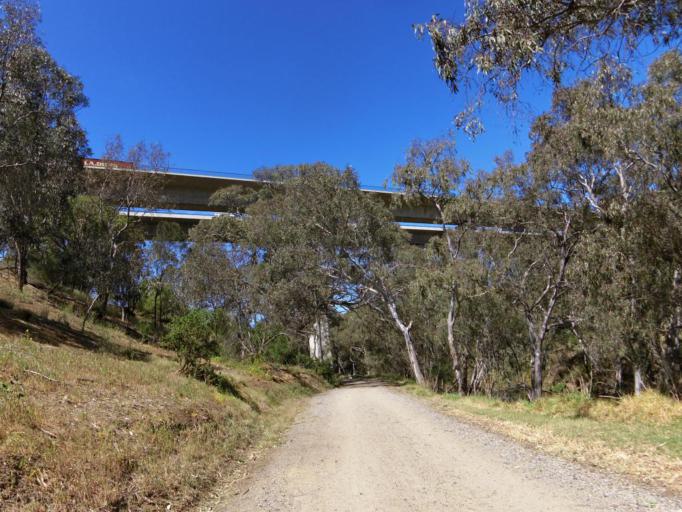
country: AU
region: Victoria
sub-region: Brimbank
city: Kealba
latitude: -37.7450
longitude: 144.8391
